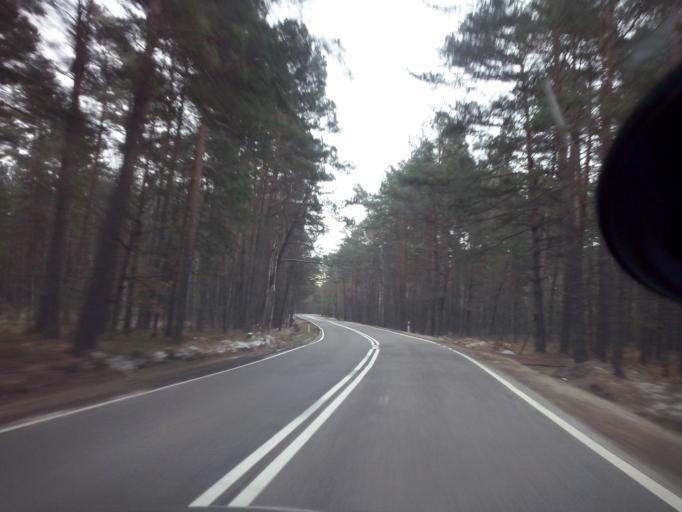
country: PL
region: Lublin Voivodeship
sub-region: Powiat bilgorajski
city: Biszcza
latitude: 50.5030
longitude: 22.5948
